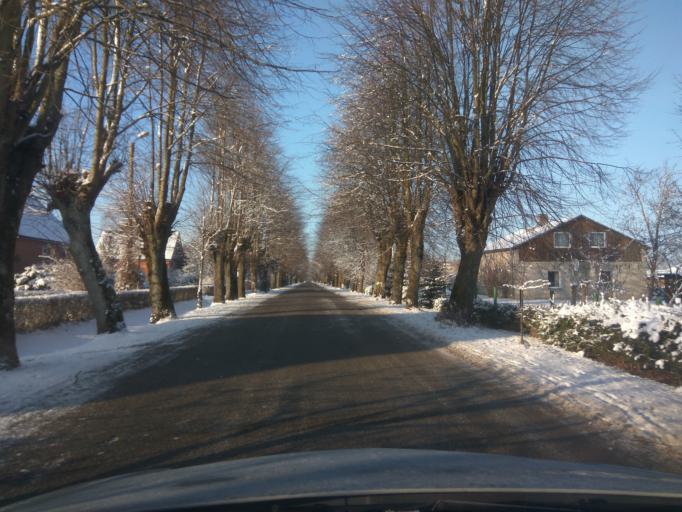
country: LV
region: Durbe
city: Liegi
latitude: 56.7321
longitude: 21.3939
